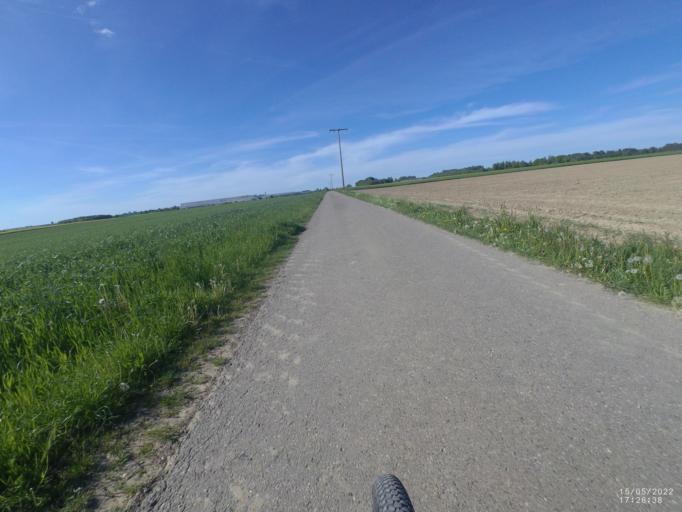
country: DE
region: Baden-Wuerttemberg
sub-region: Tuebingen Region
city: Setzingen
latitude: 48.5806
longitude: 10.1307
